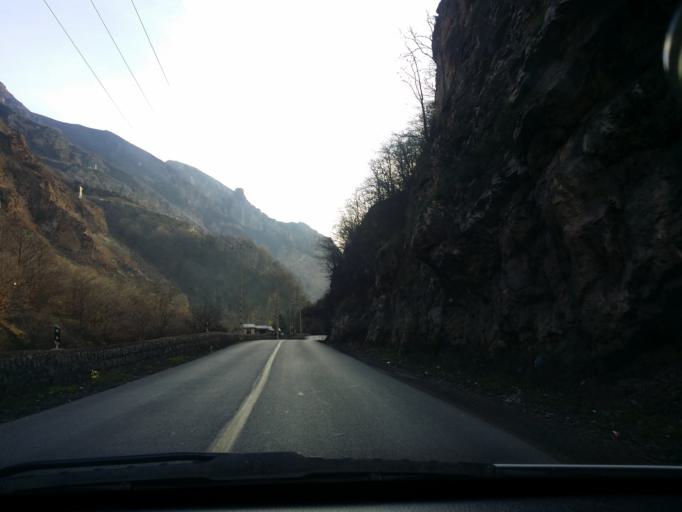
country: IR
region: Mazandaran
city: Chalus
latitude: 36.2679
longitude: 51.2533
